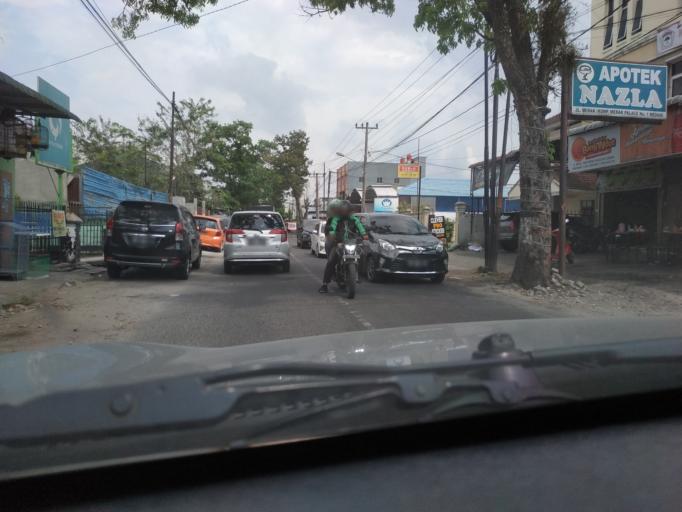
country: ID
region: North Sumatra
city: Sunggal
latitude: 3.5847
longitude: 98.6290
